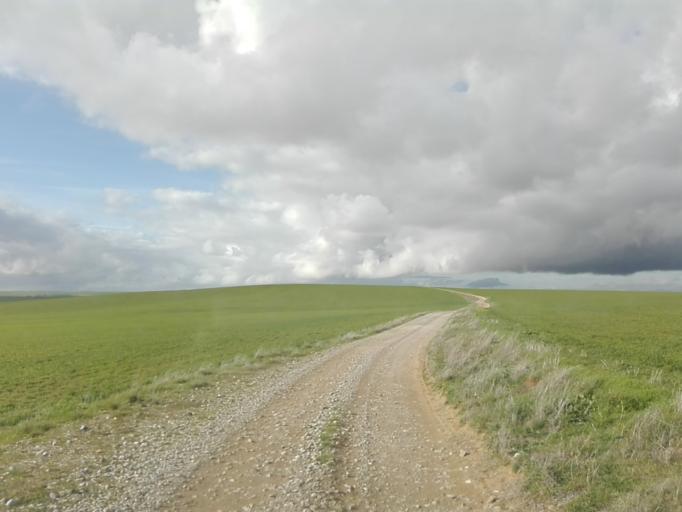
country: ES
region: Extremadura
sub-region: Provincia de Badajoz
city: Llerena
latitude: 38.2909
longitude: -5.9835
